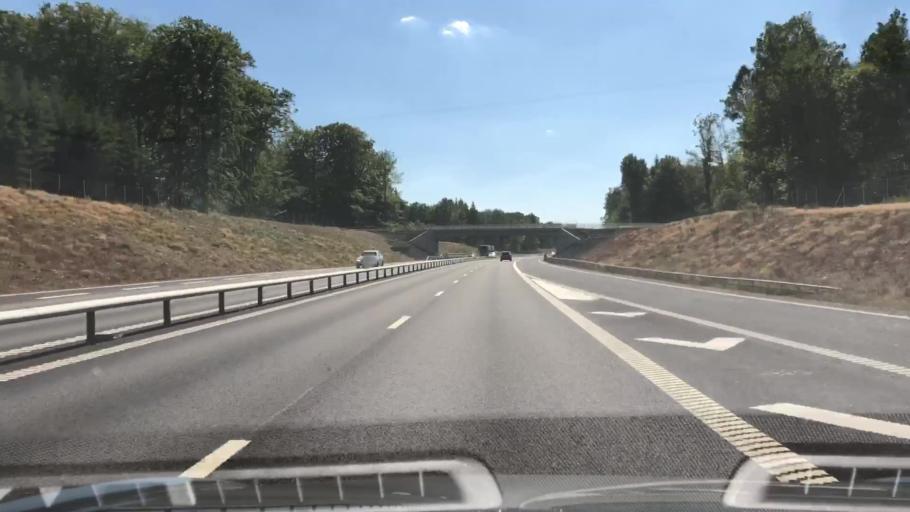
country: SE
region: Skane
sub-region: Hassleholms Kommun
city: Vinslov
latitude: 55.9346
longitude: 13.8480
